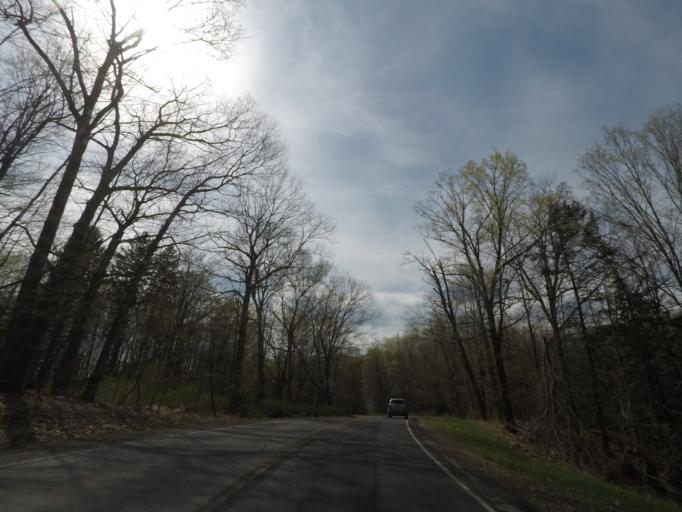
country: US
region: New York
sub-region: Columbia County
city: Chatham
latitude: 42.3349
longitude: -73.6043
